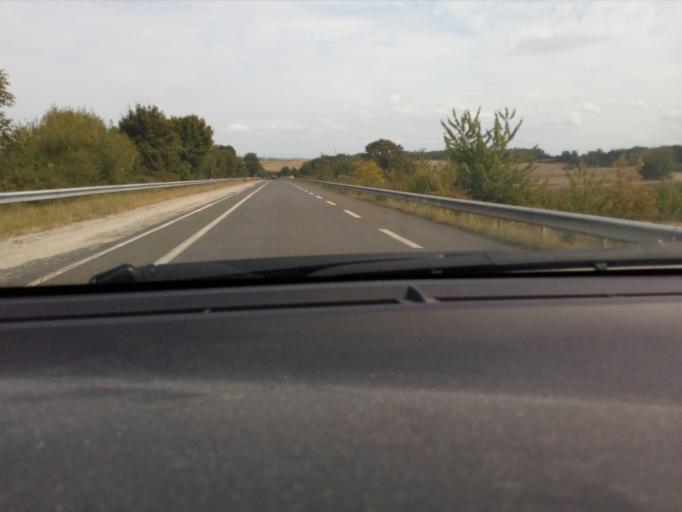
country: FR
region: Poitou-Charentes
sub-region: Departement de la Charente
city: Saint-Saturnin
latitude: 45.6704
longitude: 0.0318
